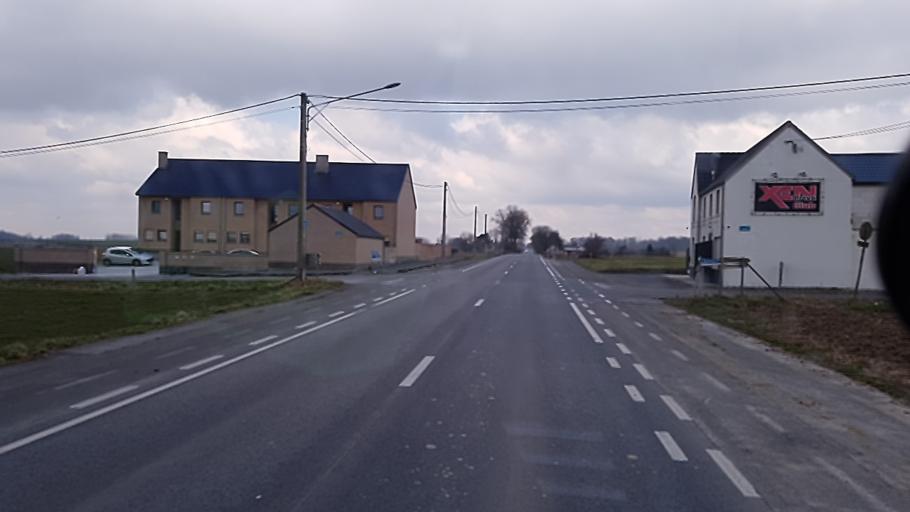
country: BE
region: Wallonia
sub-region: Province du Hainaut
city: Peruwelz
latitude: 50.5552
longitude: 3.5914
